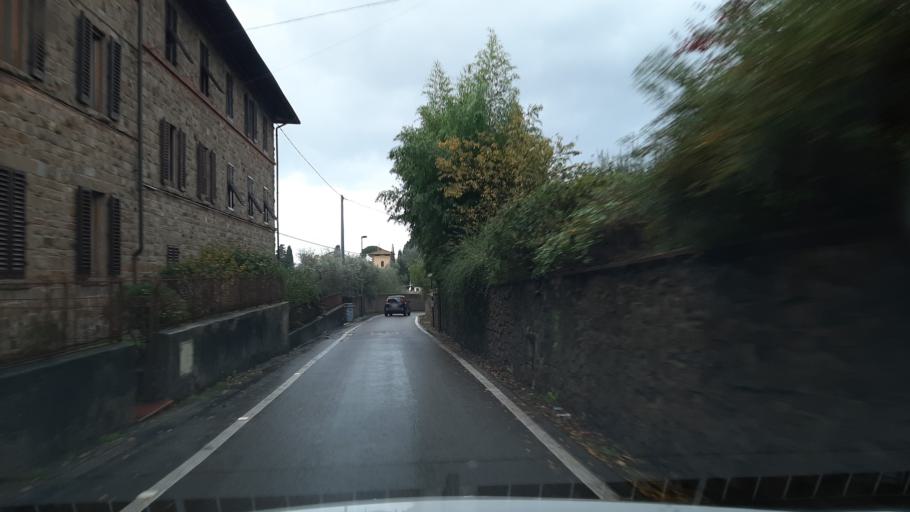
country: IT
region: Tuscany
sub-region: Province of Florence
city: Fiesole
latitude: 43.8076
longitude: 11.2669
